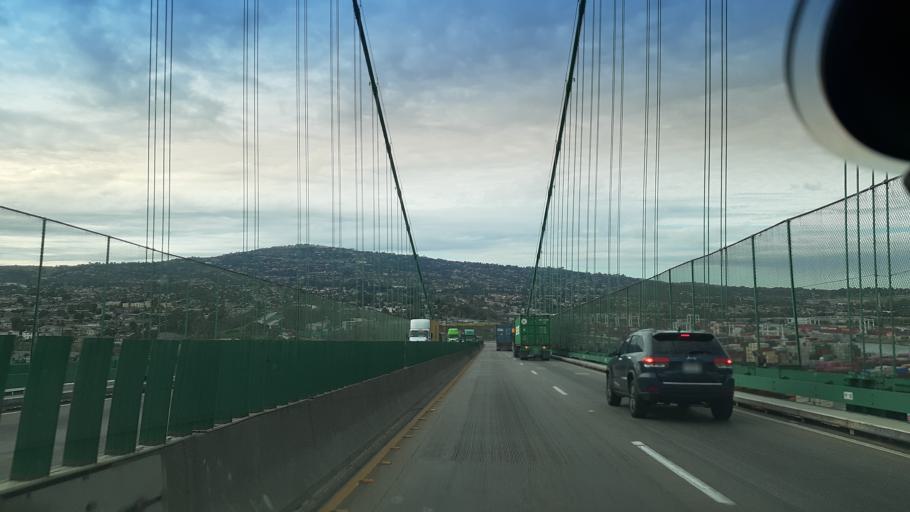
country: US
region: California
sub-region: Los Angeles County
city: San Pedro
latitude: 33.7498
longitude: -118.2738
